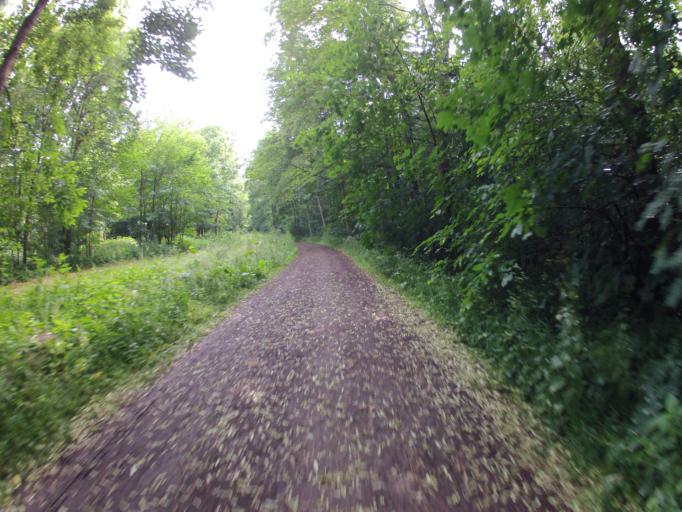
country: DE
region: Saxony
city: Markkleeberg
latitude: 51.3008
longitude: 12.3531
